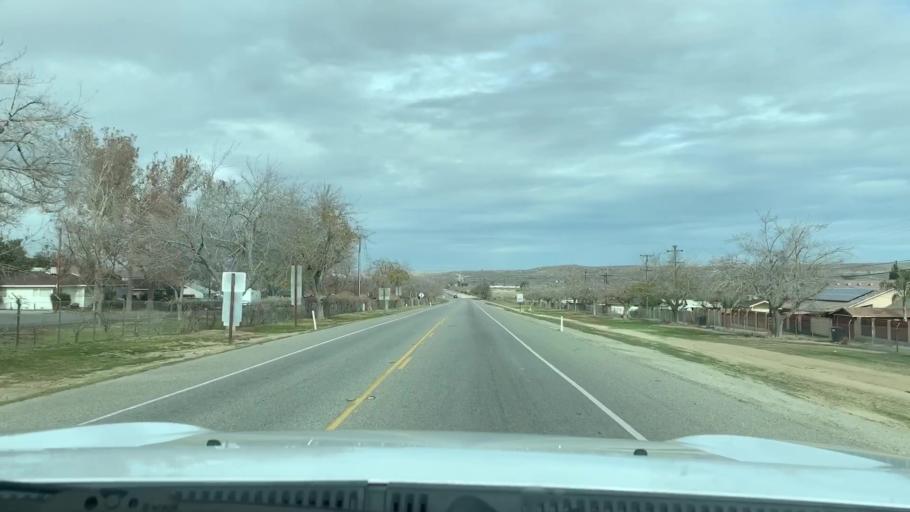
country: US
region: California
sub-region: Kern County
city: Taft
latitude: 35.1413
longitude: -119.4472
